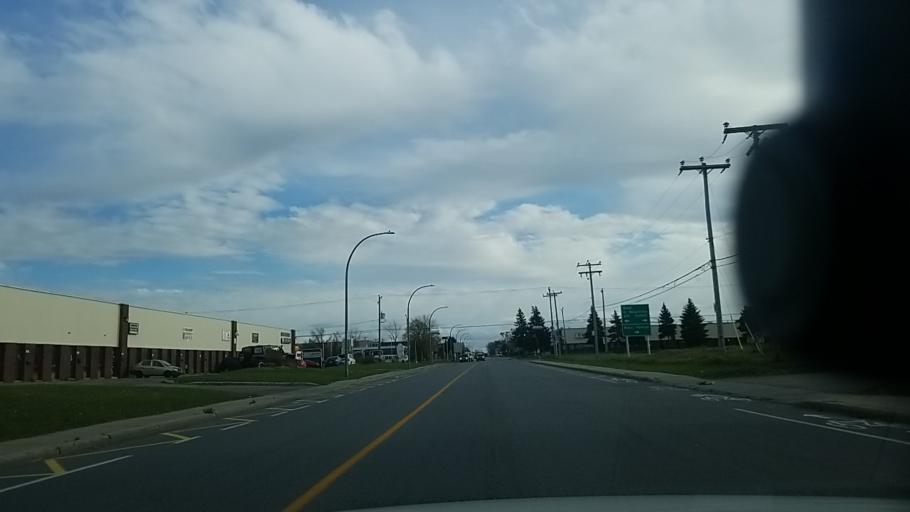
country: CA
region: Quebec
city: Dorval
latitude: 45.4973
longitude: -73.7542
